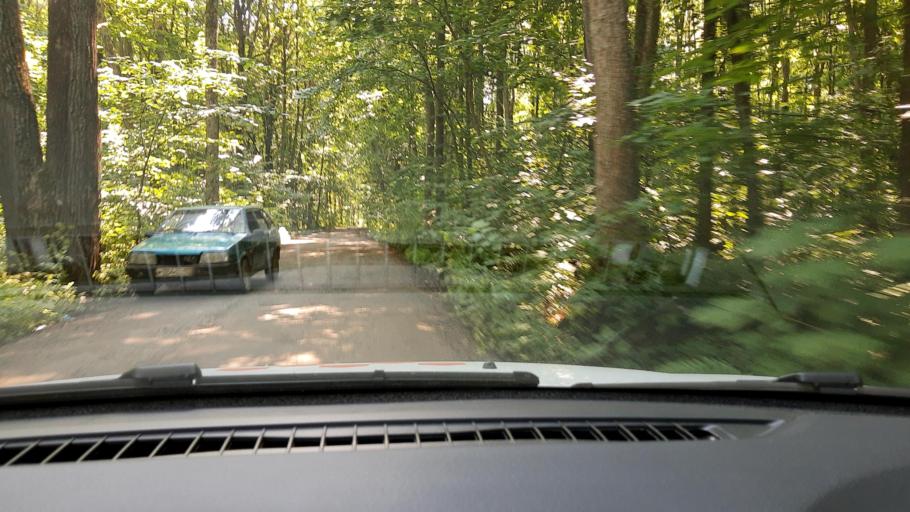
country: RU
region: Nizjnij Novgorod
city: Burevestnik
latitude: 56.0539
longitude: 43.9901
